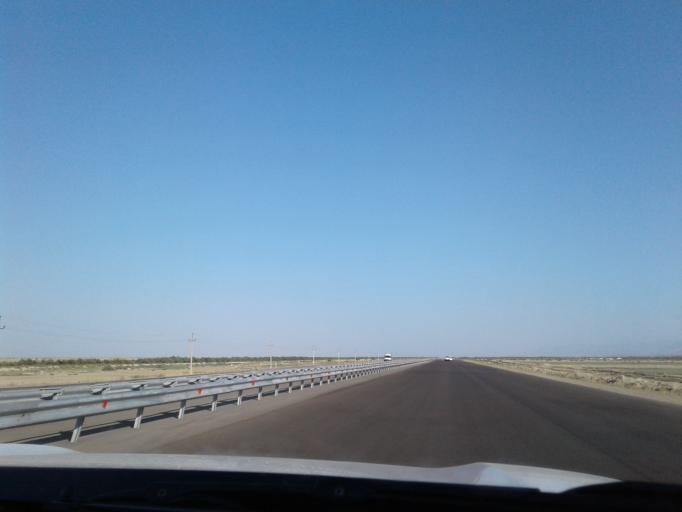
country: TM
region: Balkan
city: Serdar
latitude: 38.8990
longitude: 56.5145
